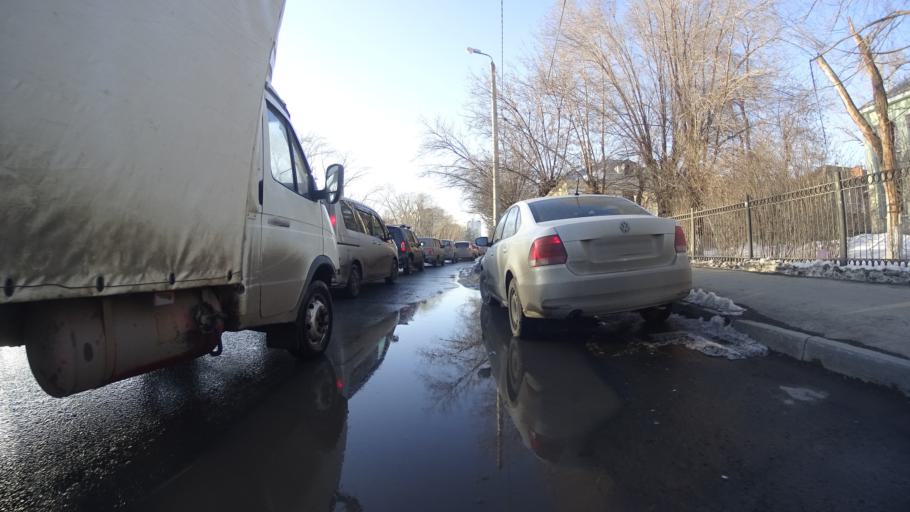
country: RU
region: Chelyabinsk
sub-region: Gorod Chelyabinsk
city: Chelyabinsk
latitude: 55.1340
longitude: 61.4594
